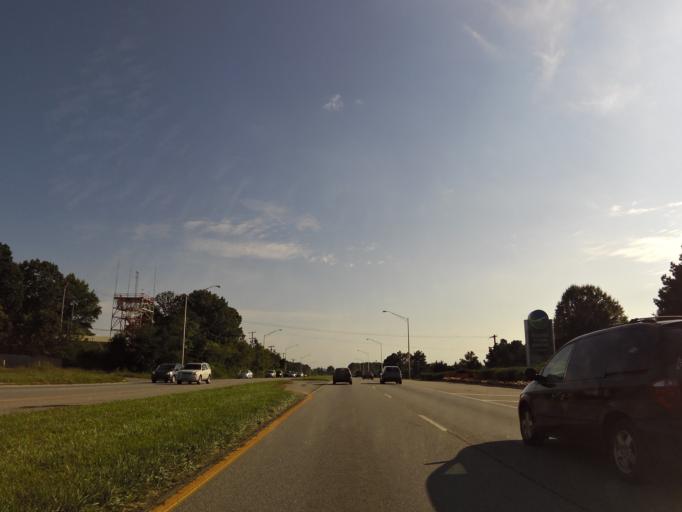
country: US
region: Tennessee
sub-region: Blount County
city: Alcoa
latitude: 35.8093
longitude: -83.9850
